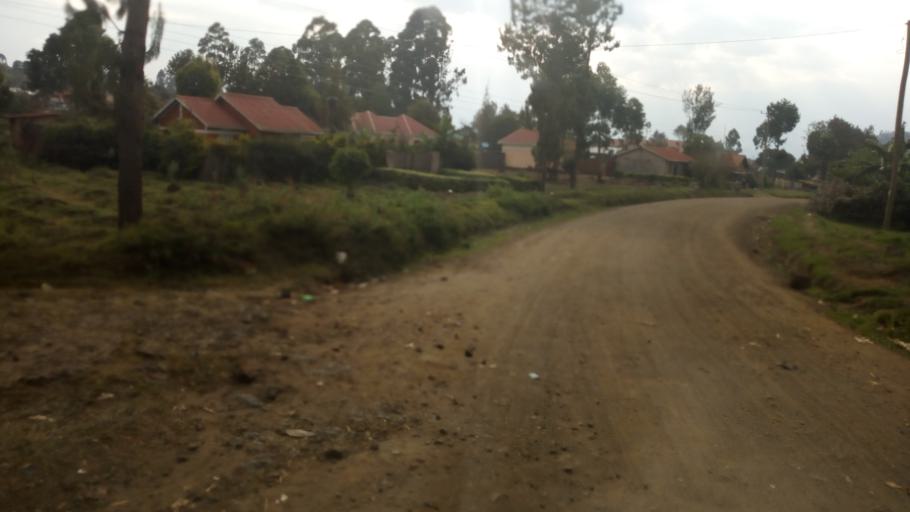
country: UG
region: Western Region
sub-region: Kisoro District
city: Kisoro
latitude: -1.2912
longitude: 29.6931
